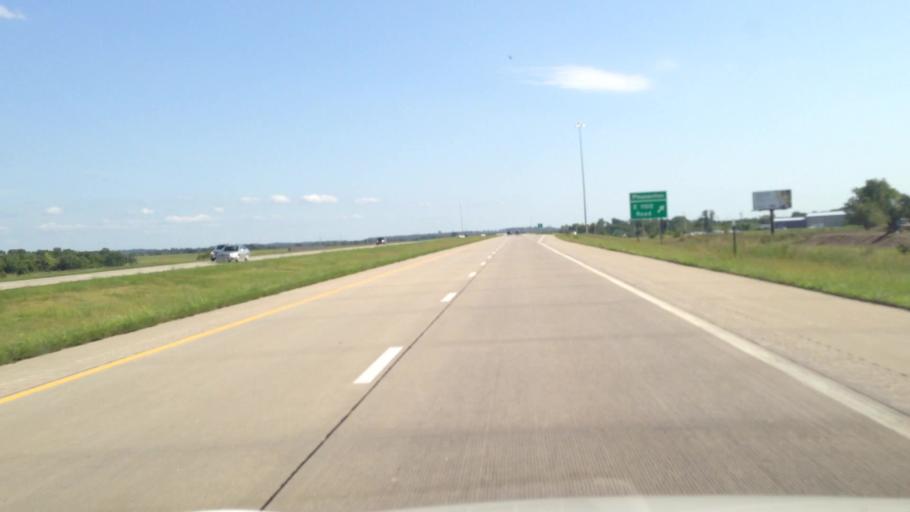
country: US
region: Kansas
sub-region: Linn County
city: Pleasanton
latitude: 38.1871
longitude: -94.7028
